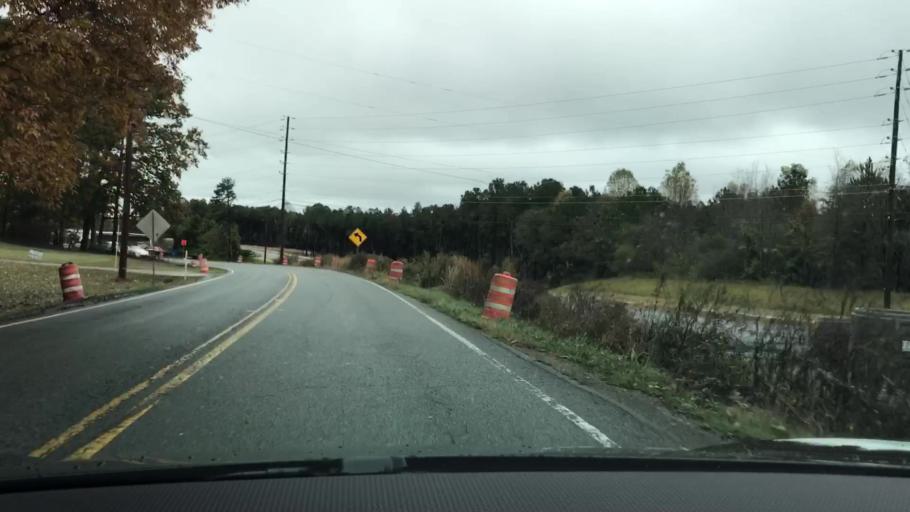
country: US
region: Georgia
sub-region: Gwinnett County
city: Buford
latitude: 34.1575
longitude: -83.9899
